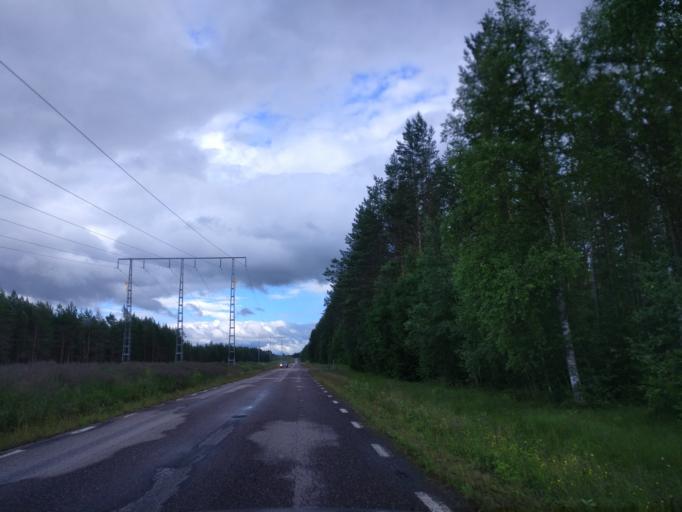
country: SE
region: Vaermland
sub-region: Hagfors Kommun
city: Hagfors
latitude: 60.0399
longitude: 13.5396
